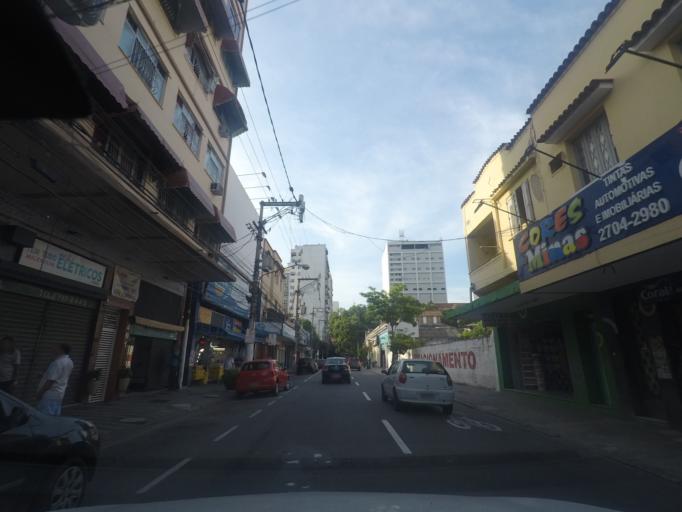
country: BR
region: Rio de Janeiro
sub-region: Niteroi
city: Niteroi
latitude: -22.8902
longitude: -43.1202
